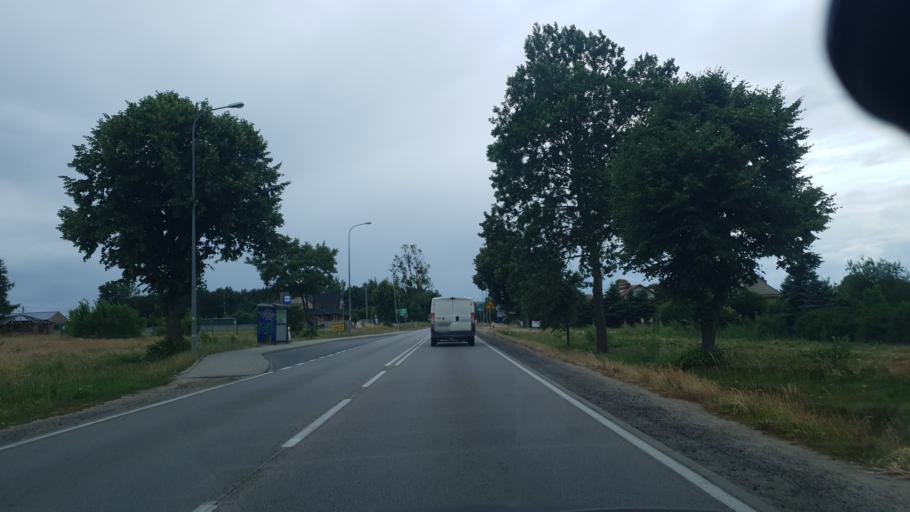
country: PL
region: Pomeranian Voivodeship
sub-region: Powiat kartuski
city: Banino
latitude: 54.4035
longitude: 18.3627
